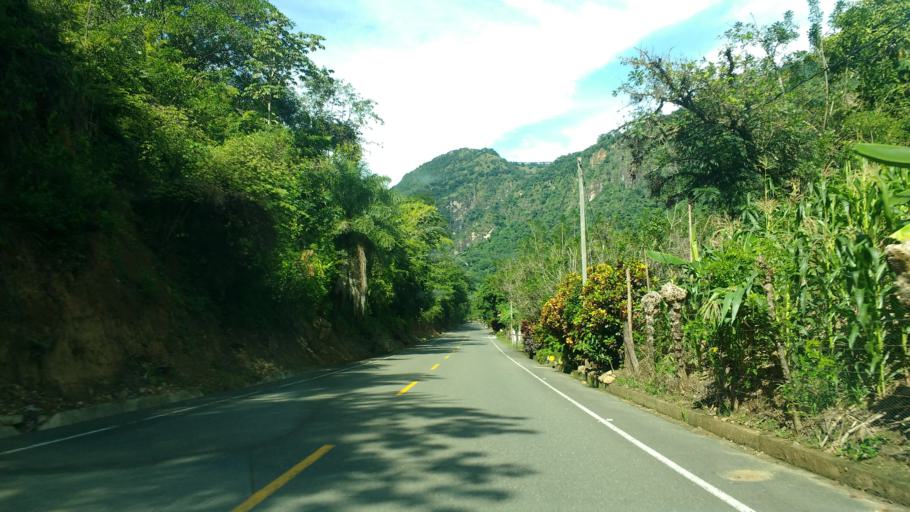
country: CO
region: Antioquia
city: Concordia
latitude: 6.0610
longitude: -75.8651
